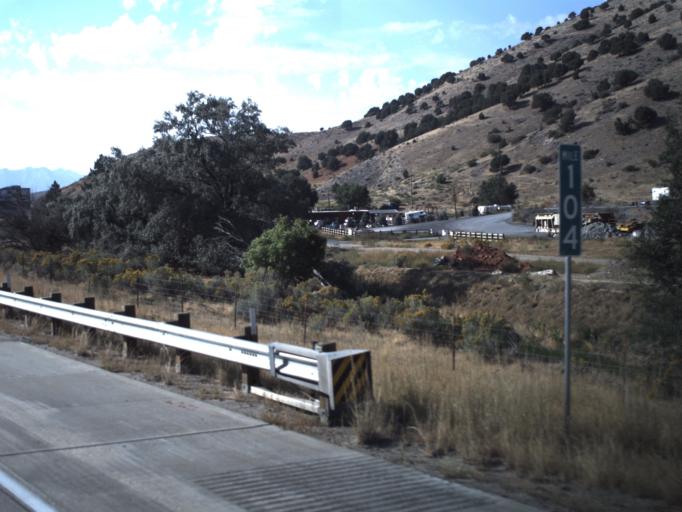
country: US
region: Utah
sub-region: Morgan County
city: Morgan
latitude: 41.0418
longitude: -111.6639
